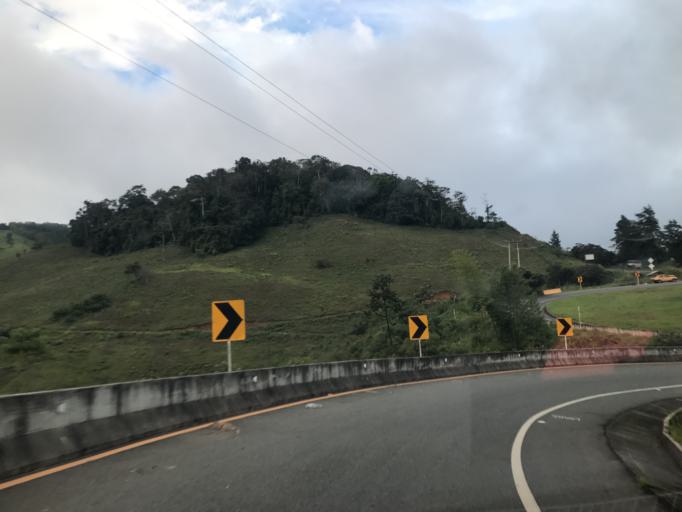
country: CO
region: Valle del Cauca
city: Restrepo
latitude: 3.8524
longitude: -76.5512
